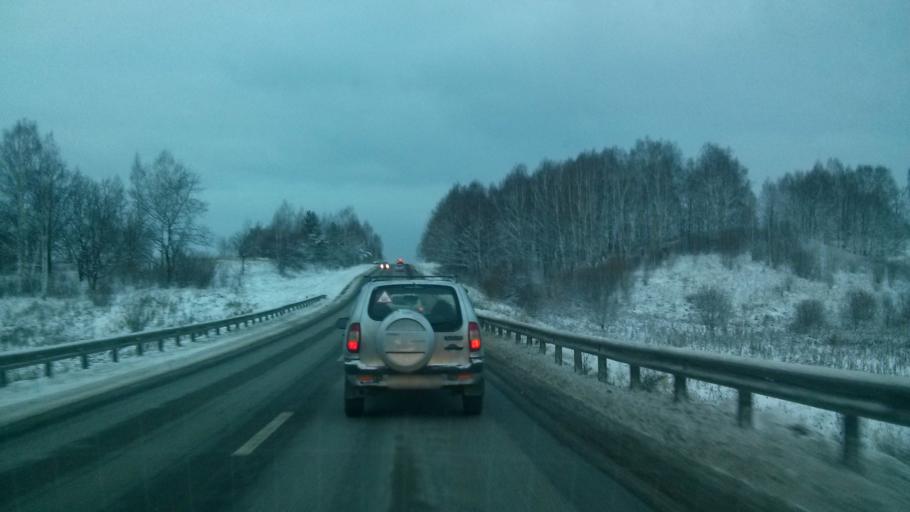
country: RU
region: Nizjnij Novgorod
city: Bogorodsk
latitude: 56.1022
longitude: 43.5855
